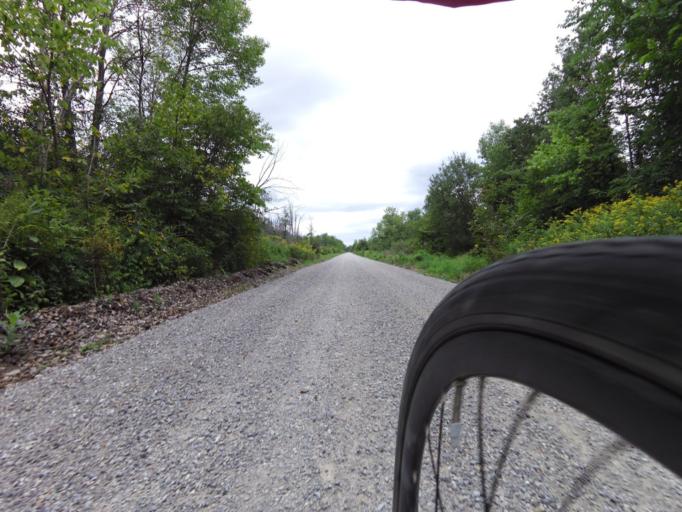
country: CA
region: Ontario
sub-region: Lanark County
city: Smiths Falls
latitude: 44.9440
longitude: -76.0409
